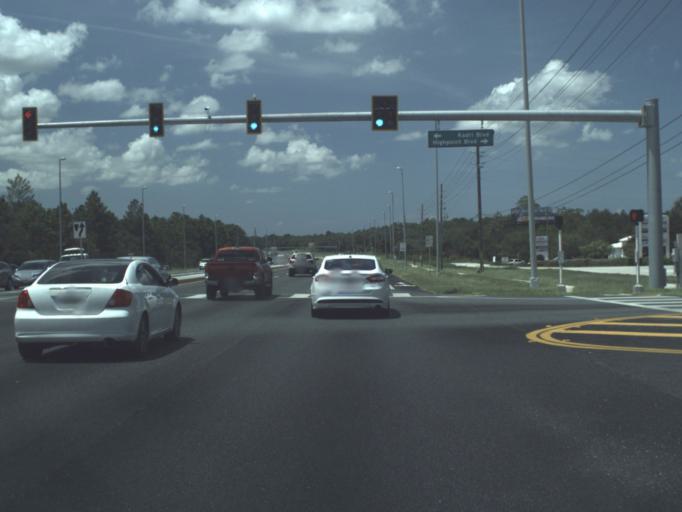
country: US
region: Florida
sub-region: Hernando County
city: High Point
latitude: 28.5336
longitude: -82.5276
